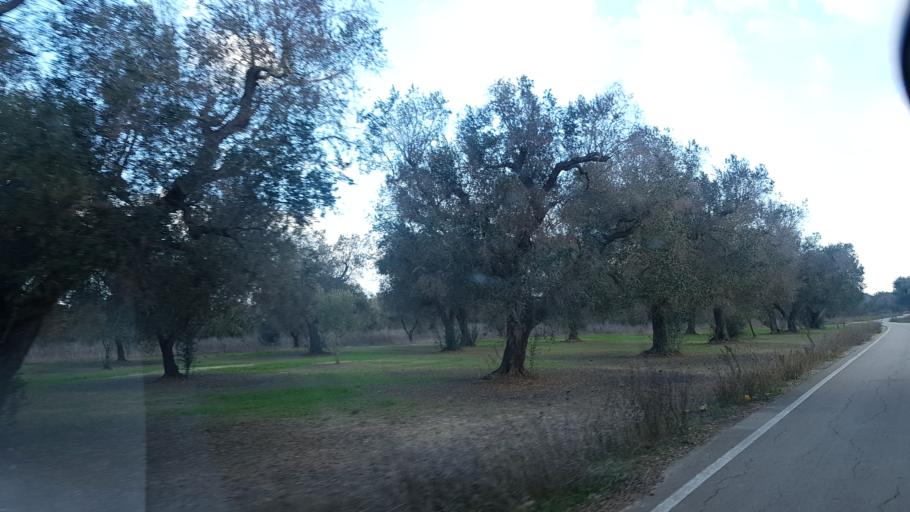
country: IT
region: Apulia
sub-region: Provincia di Brindisi
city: San Pietro Vernotico
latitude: 40.5151
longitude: 18.0140
